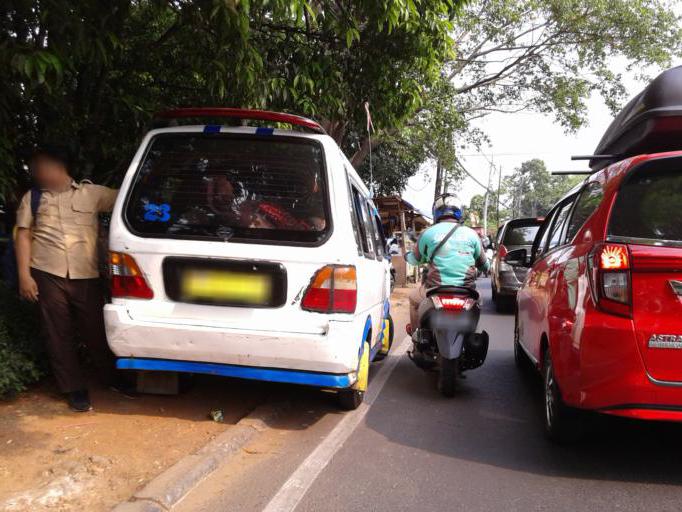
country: ID
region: West Java
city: Pamulang
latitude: -6.3148
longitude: 106.7822
